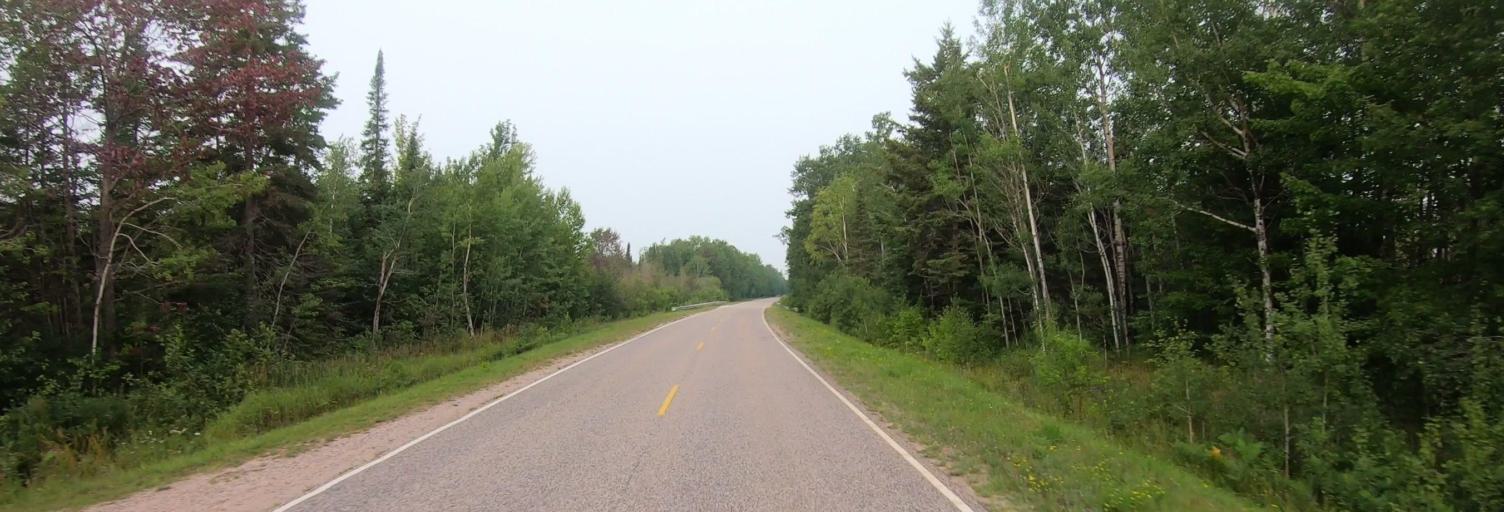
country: US
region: Michigan
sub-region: Chippewa County
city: Sault Ste. Marie
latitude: 46.4645
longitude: -84.8971
